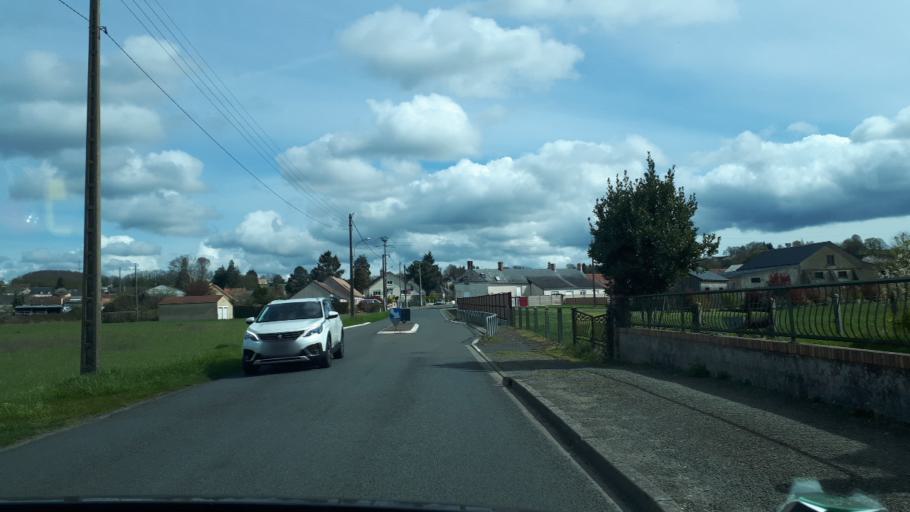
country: FR
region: Pays de la Loire
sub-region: Departement de la Sarthe
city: Brette-les-Pins
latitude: 47.8684
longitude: 0.3275
